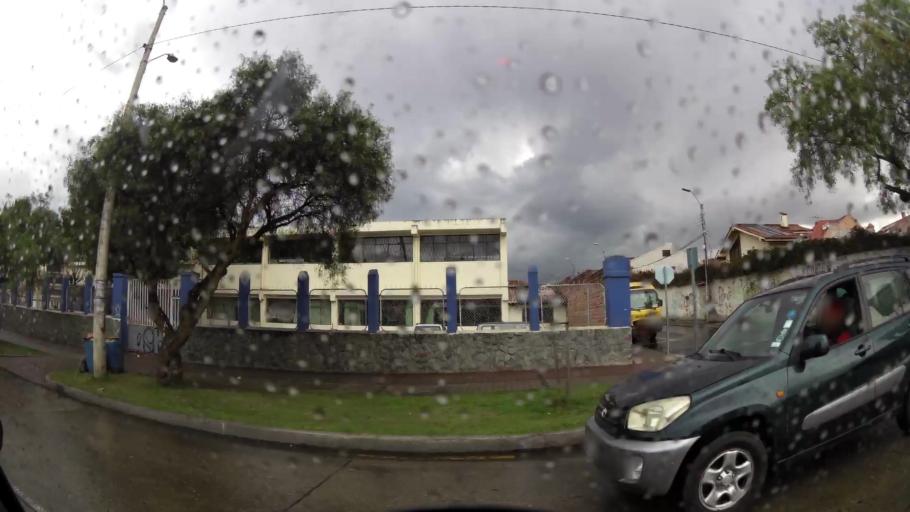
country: EC
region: Azuay
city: Cuenca
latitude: -2.9017
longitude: -79.0152
